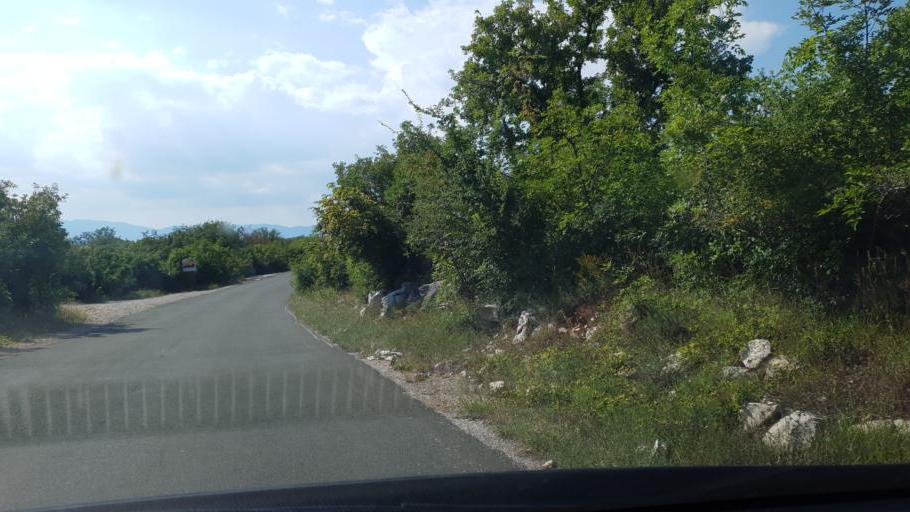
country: HR
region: Primorsko-Goranska
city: Omisalj
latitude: 45.1991
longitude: 14.5746
